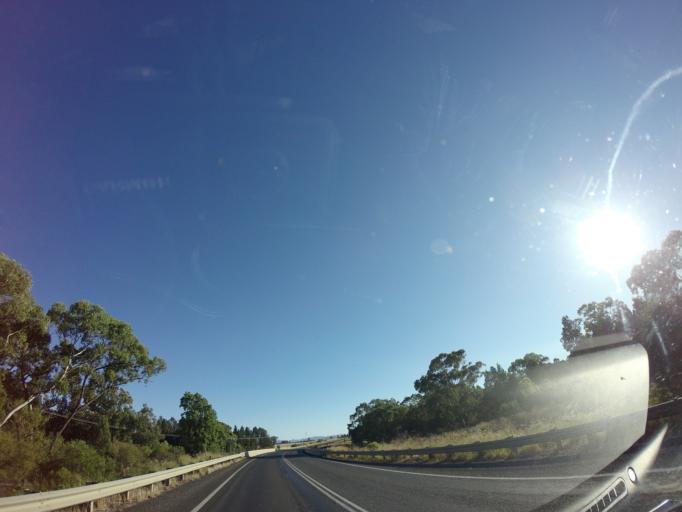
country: AU
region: New South Wales
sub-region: Gilgandra
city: Gilgandra
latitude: -31.5685
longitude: 148.7865
